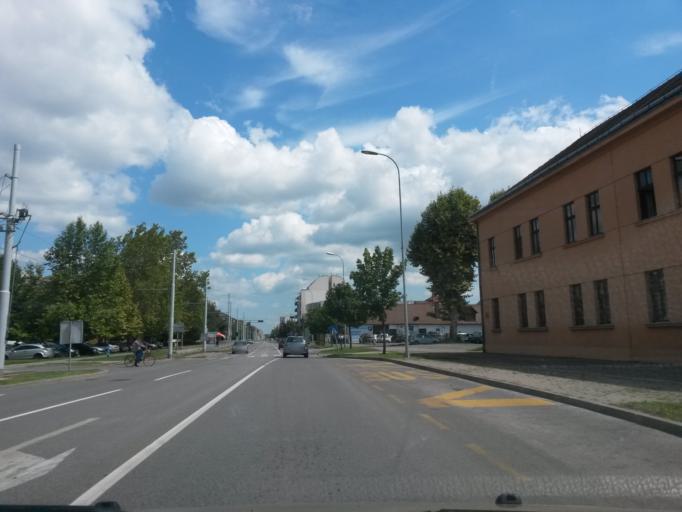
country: HR
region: Osjecko-Baranjska
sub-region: Grad Osijek
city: Osijek
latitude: 45.5488
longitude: 18.6939
